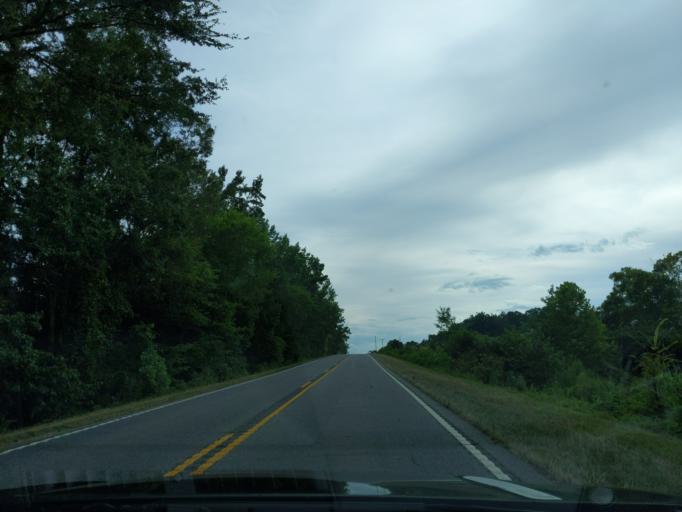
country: US
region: North Carolina
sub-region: Cabarrus County
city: Mount Pleasant
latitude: 35.4320
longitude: -80.4024
